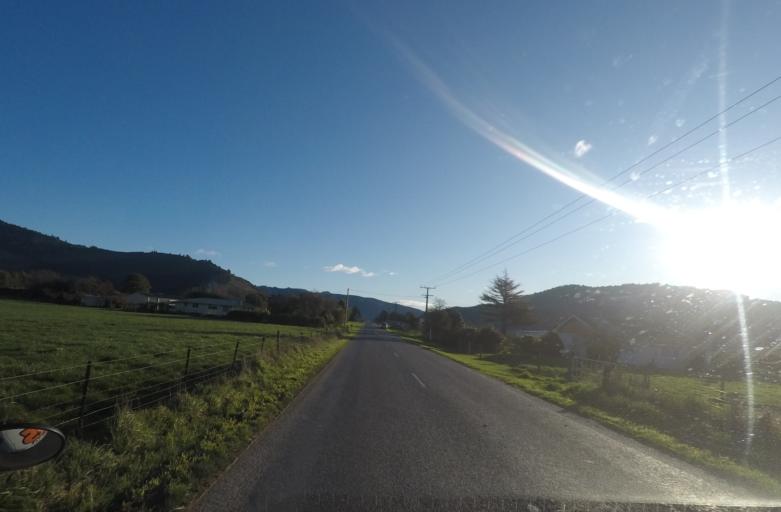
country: NZ
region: Marlborough
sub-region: Marlborough District
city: Picton
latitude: -41.2895
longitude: 173.8700
